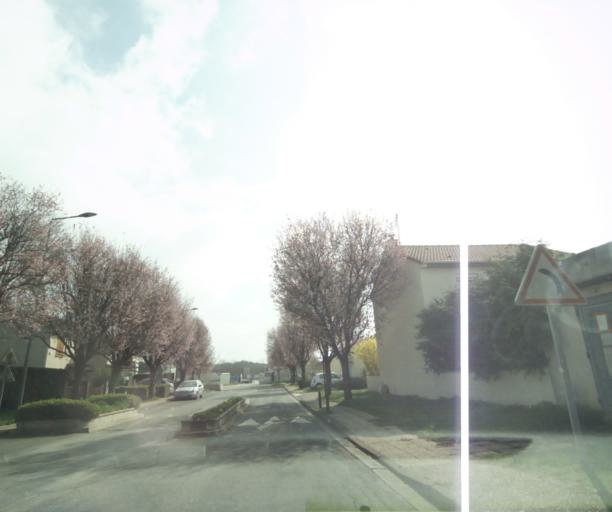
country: FR
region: Ile-de-France
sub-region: Departement du Val-d'Oise
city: Vaureal
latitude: 49.0436
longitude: 2.0226
